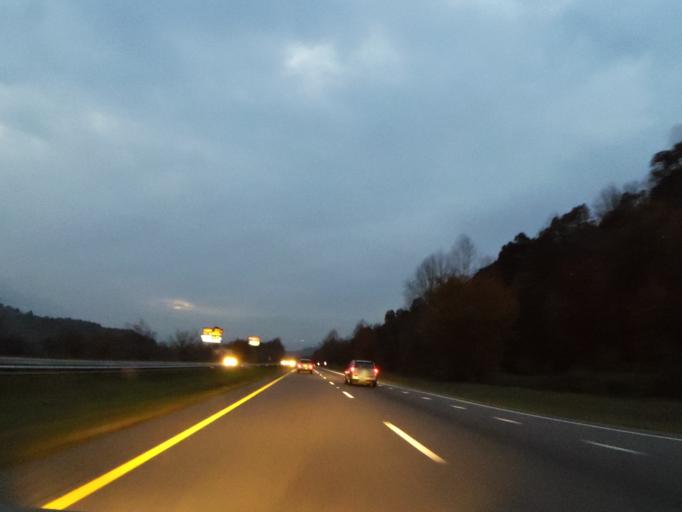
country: US
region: North Carolina
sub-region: McDowell County
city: West Marion
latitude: 35.6389
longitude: -82.1462
